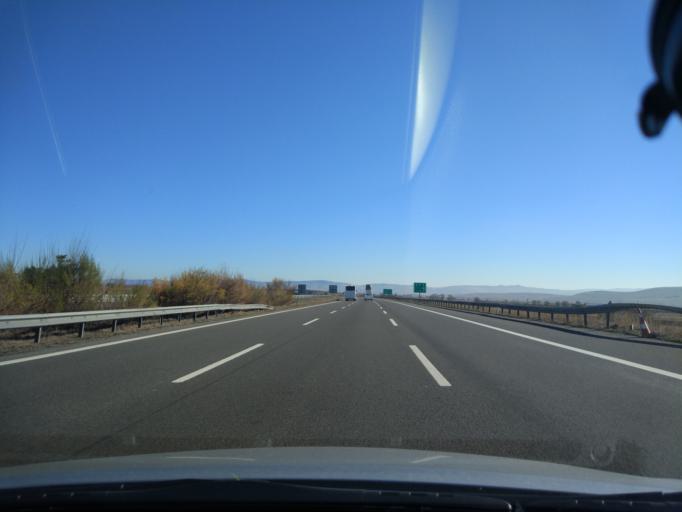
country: TR
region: Bolu
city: Dortdivan
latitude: 40.7408
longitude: 32.1296
